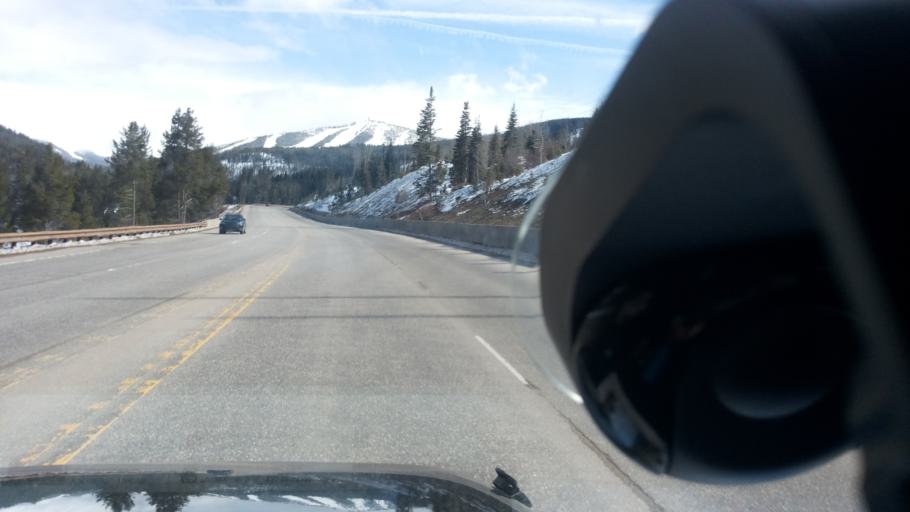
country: US
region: Colorado
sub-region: Grand County
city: Fraser
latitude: 39.9112
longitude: -105.7820
